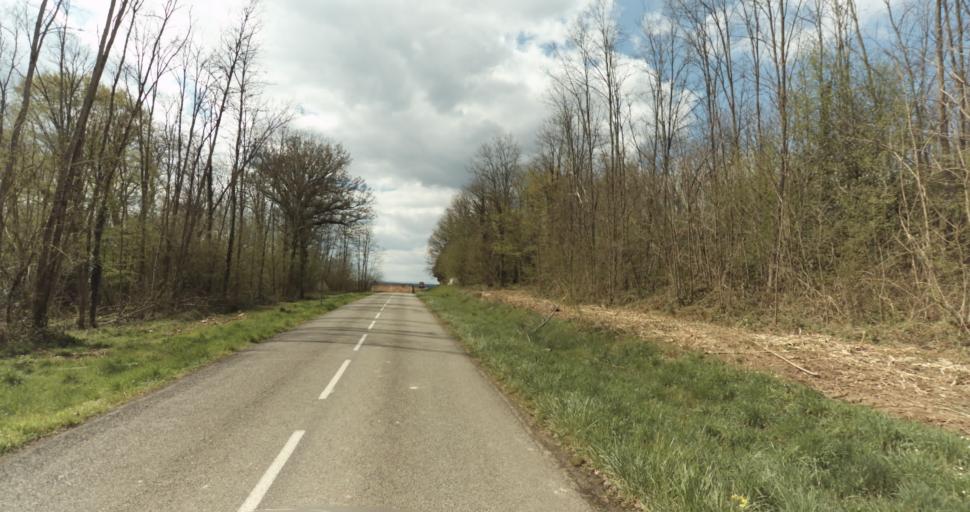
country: FR
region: Bourgogne
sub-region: Departement de la Cote-d'Or
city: Auxonne
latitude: 47.1933
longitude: 5.4331
